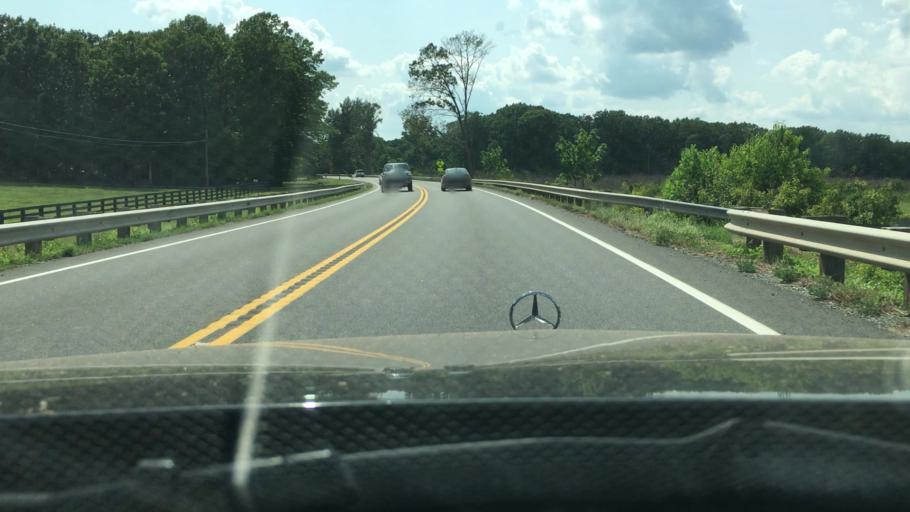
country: US
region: Virginia
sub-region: Orange County
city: Orange
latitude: 38.2721
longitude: -77.9057
